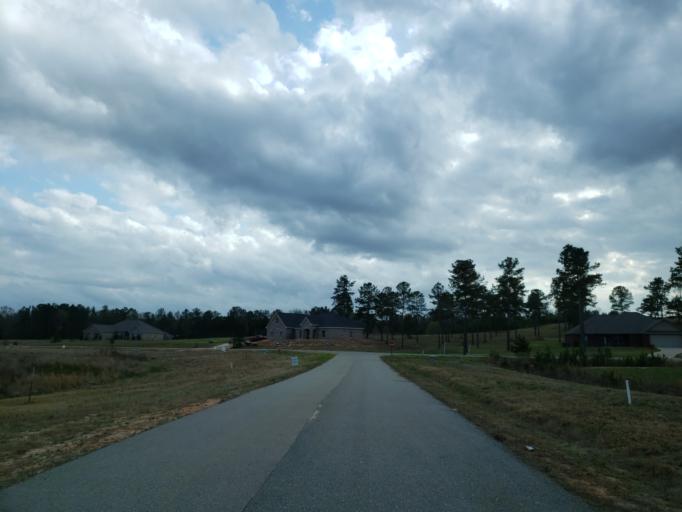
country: US
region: Mississippi
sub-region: Jones County
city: Ellisville
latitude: 31.5644
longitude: -89.2488
